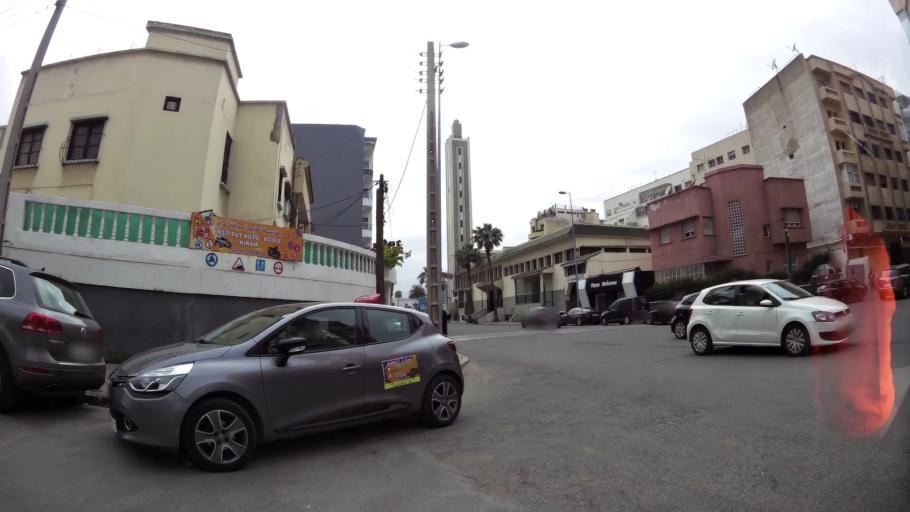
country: MA
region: Grand Casablanca
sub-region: Casablanca
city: Casablanca
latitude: 33.5697
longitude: -7.6103
